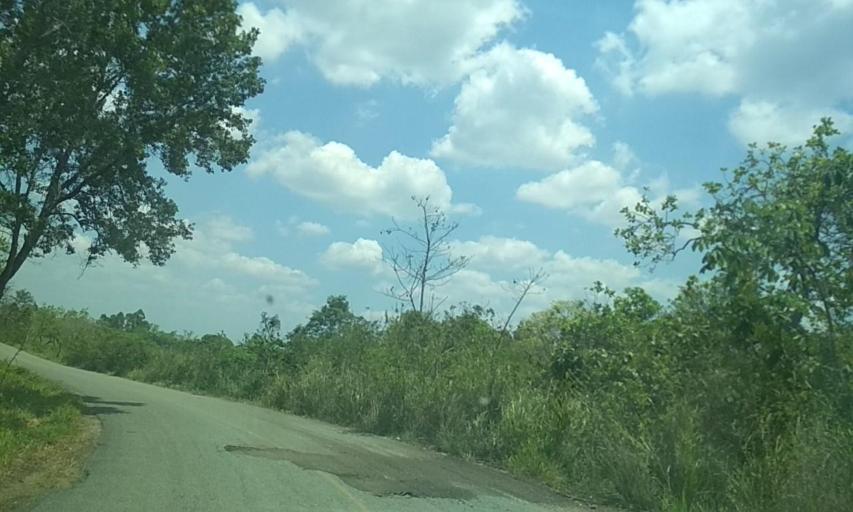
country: MX
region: Tabasco
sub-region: Huimanguillo
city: Francisco Rueda
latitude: 17.7788
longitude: -93.8266
